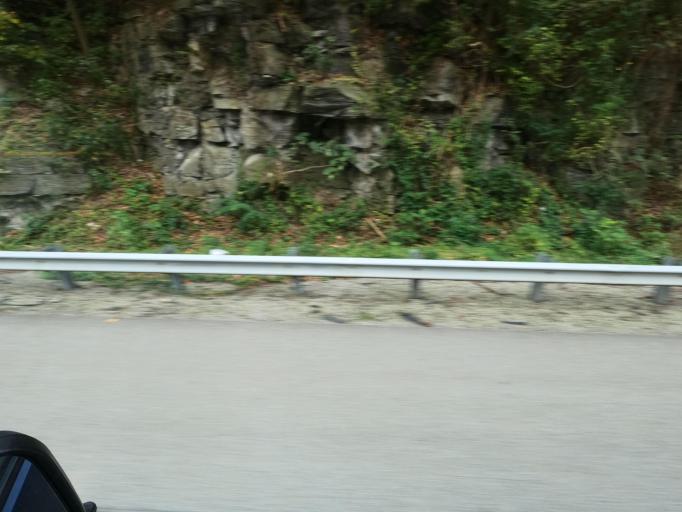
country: US
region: Tennessee
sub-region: Dickson County
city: White Bluff
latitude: 36.0280
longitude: -87.2138
